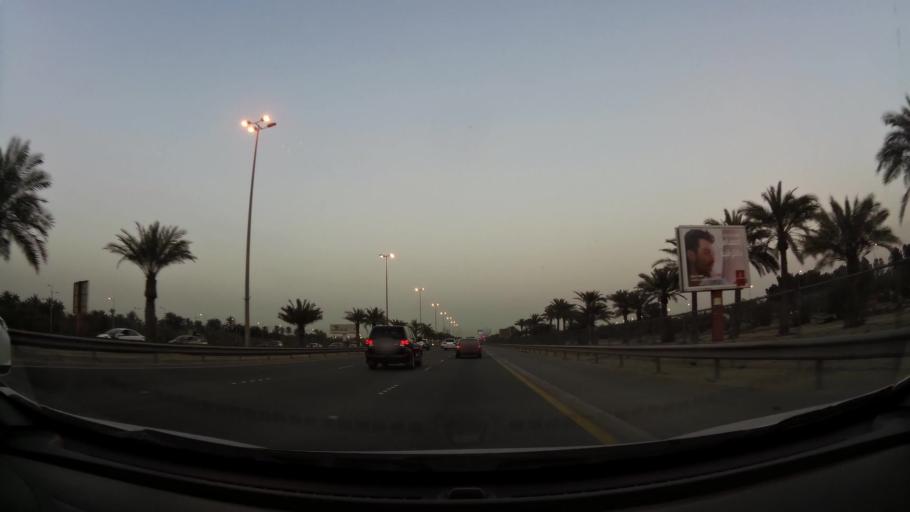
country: BH
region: Manama
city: Jidd Hafs
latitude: 26.1971
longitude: 50.5487
